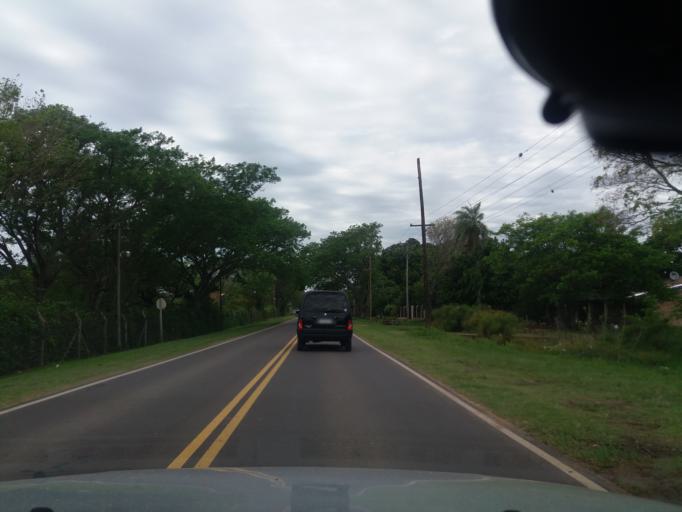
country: AR
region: Corrientes
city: Corrientes
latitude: -27.4507
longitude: -58.7367
